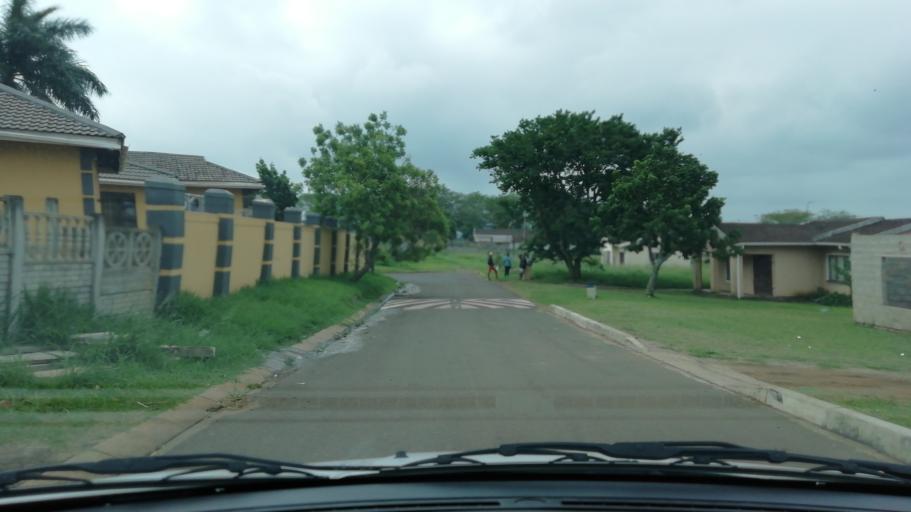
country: ZA
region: KwaZulu-Natal
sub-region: uThungulu District Municipality
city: Empangeni
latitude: -28.7367
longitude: 31.8784
